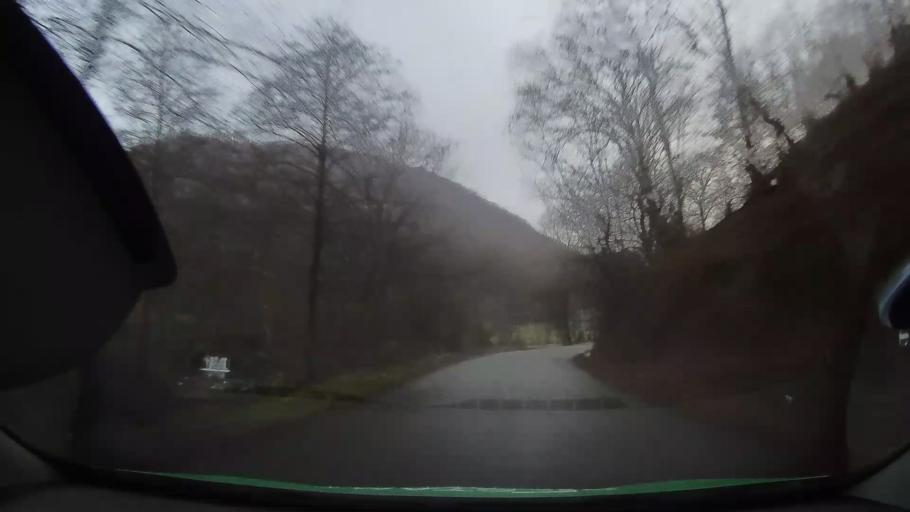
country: RO
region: Hunedoara
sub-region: Comuna Ribita
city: Ribita
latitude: 46.2718
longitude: 22.7422
